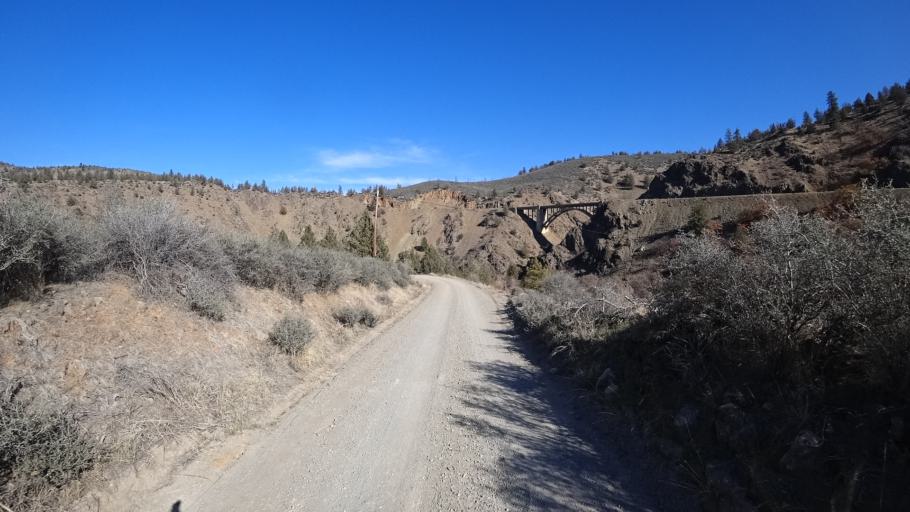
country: US
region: California
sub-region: Siskiyou County
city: Yreka
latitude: 41.8015
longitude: -122.6020
